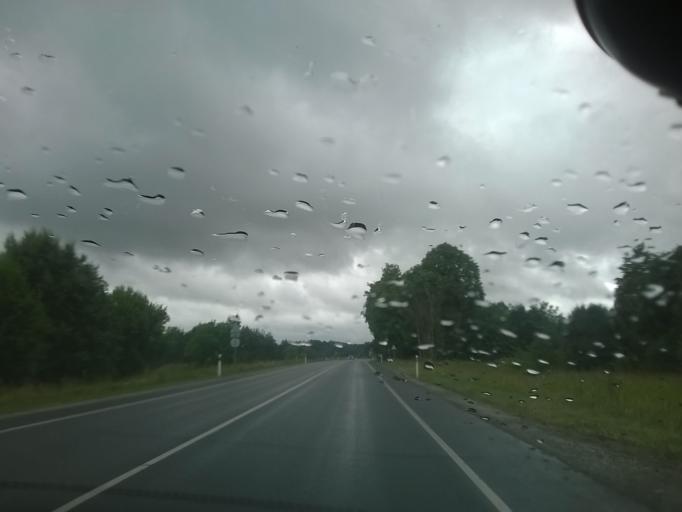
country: EE
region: Harju
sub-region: Keila linn
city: Keila
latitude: 59.3065
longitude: 24.3877
